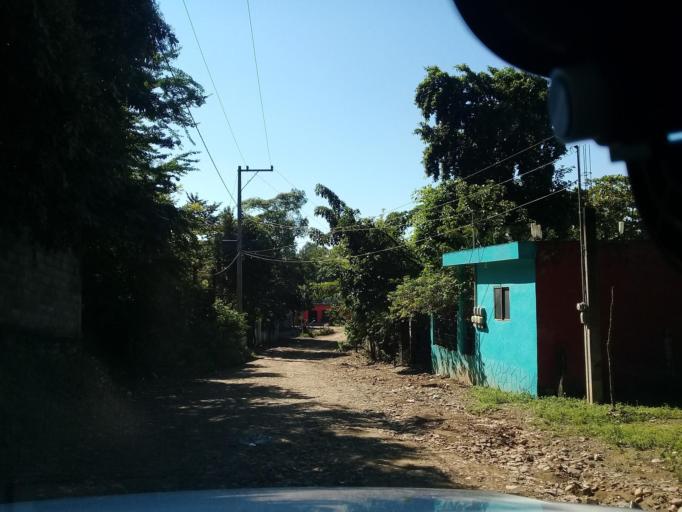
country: MX
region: Hidalgo
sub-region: Huejutla de Reyes
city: Huejutla de Reyes
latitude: 21.1619
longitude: -98.4130
